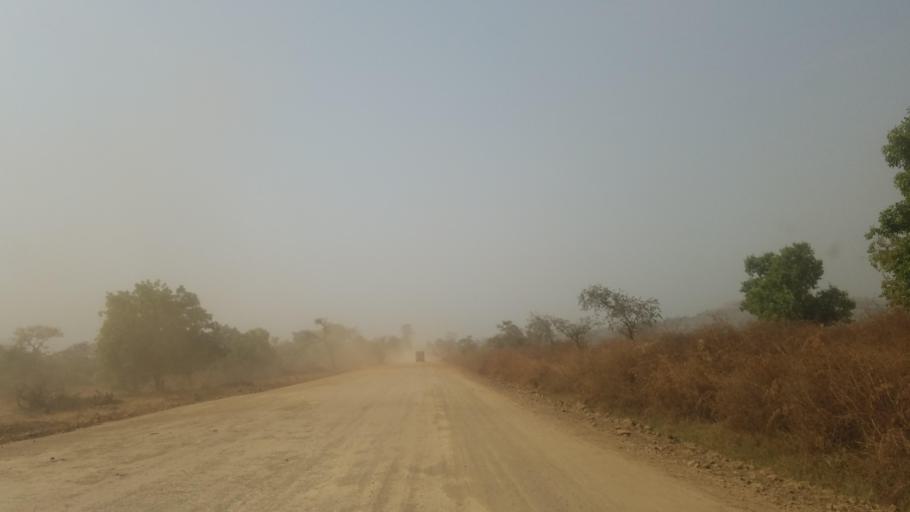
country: ET
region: Amhara
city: Bure
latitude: 10.9363
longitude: 36.4708
